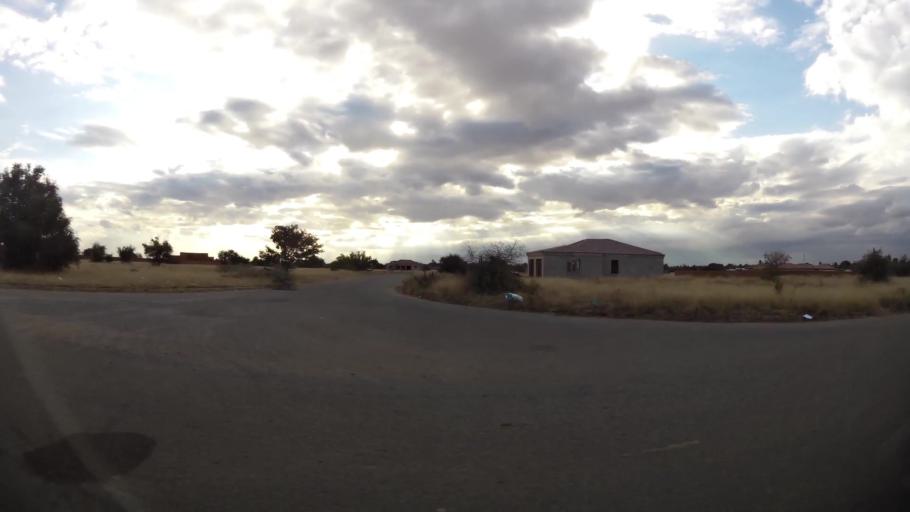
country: ZA
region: Orange Free State
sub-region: Lejweleputswa District Municipality
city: Welkom
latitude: -28.0055
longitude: 26.7327
